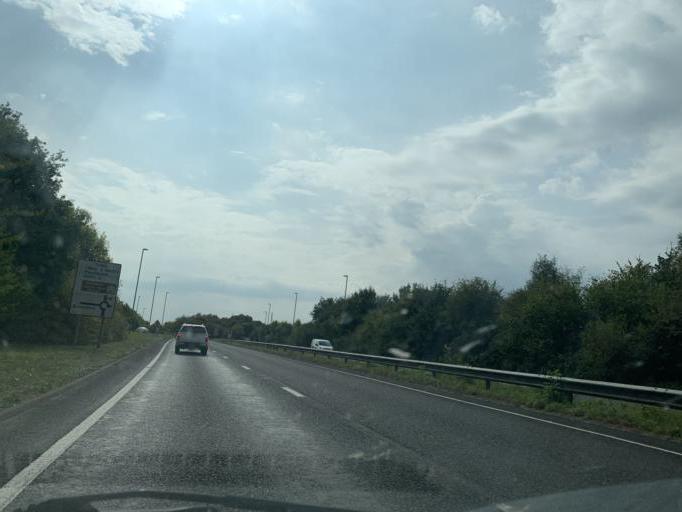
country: GB
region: England
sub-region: Hampshire
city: Totton
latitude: 50.9258
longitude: -1.5253
